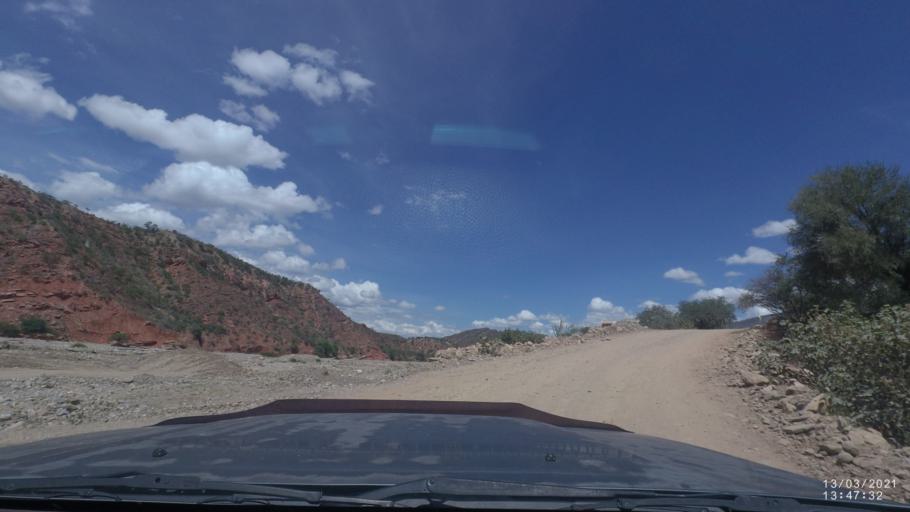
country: BO
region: Cochabamba
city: Cliza
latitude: -17.9338
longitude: -65.8678
